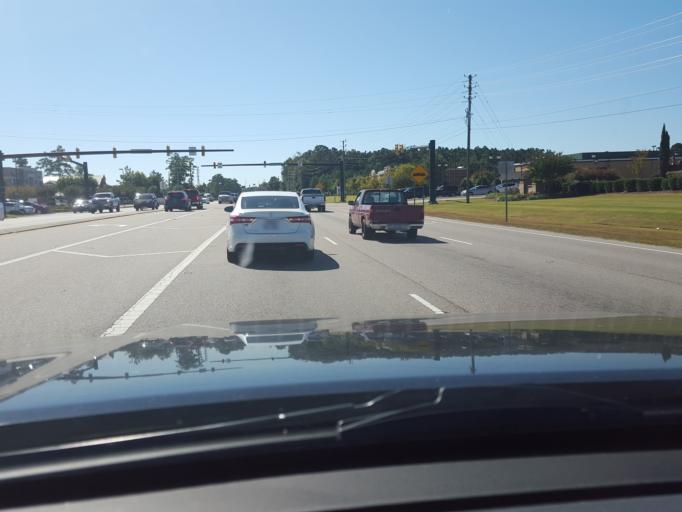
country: US
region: North Carolina
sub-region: New Hanover County
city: Seagate
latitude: 34.2359
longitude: -77.8287
